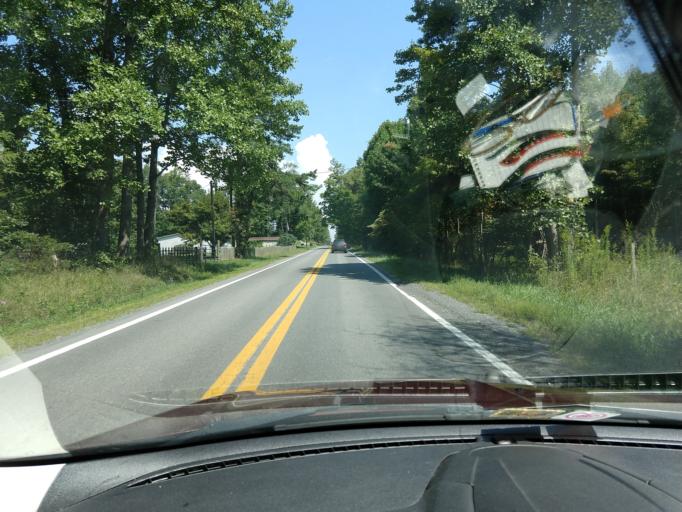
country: US
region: West Virginia
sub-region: Greenbrier County
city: Fairlea
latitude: 37.8349
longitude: -80.5556
